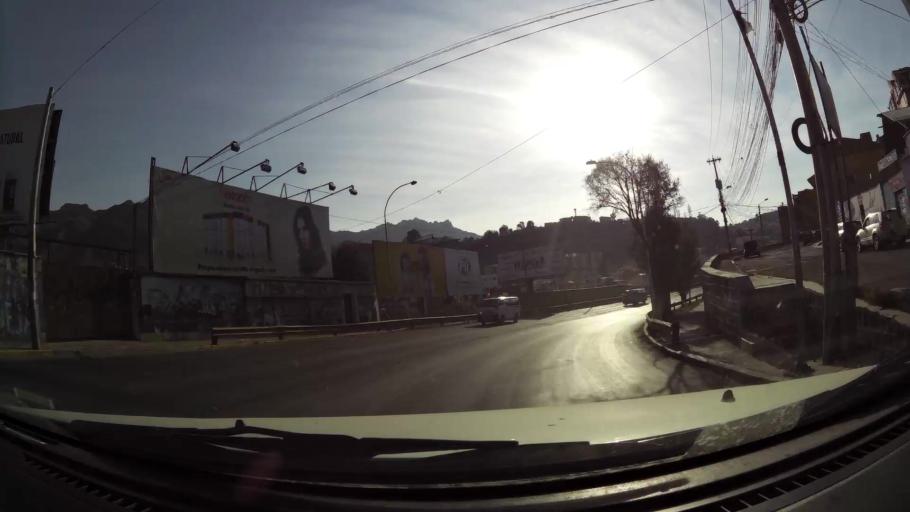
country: BO
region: La Paz
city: La Paz
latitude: -16.5417
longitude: -68.0934
